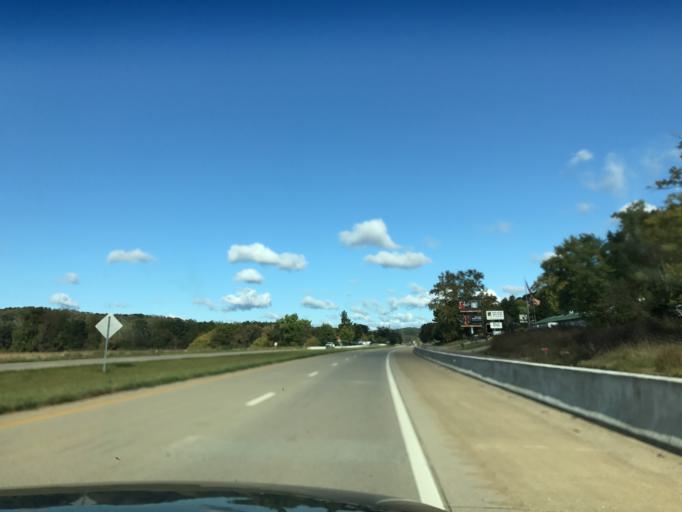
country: US
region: Ohio
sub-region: Athens County
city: Athens
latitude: 39.3131
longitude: -81.9812
